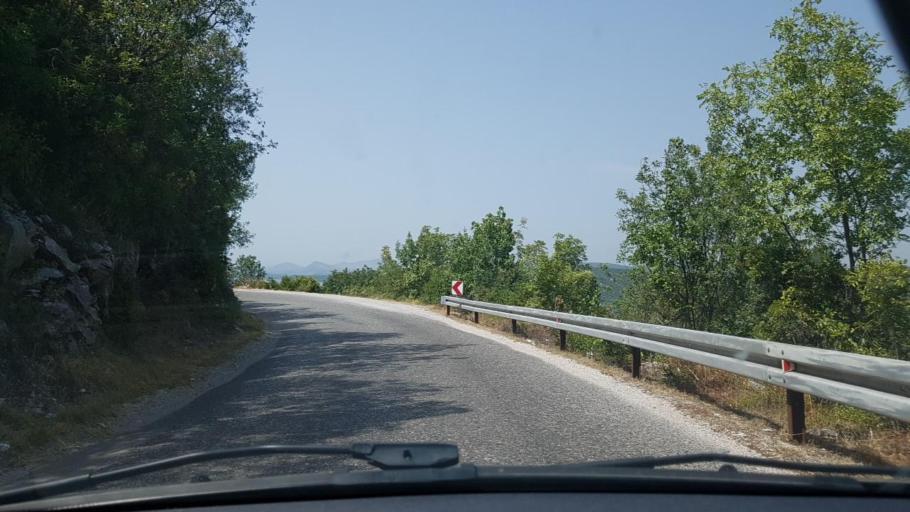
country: BA
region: Federation of Bosnia and Herzegovina
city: Tasovcici
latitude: 43.0132
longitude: 17.7877
